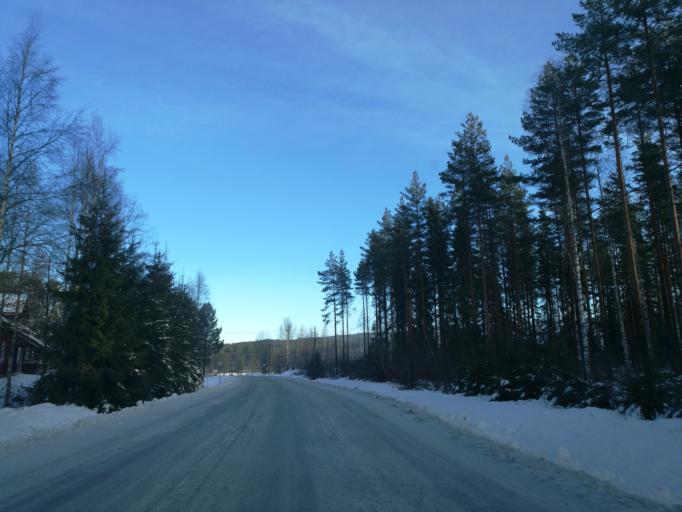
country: NO
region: Hedmark
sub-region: Grue
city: Kirkenaer
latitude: 60.3581
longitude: 12.3459
